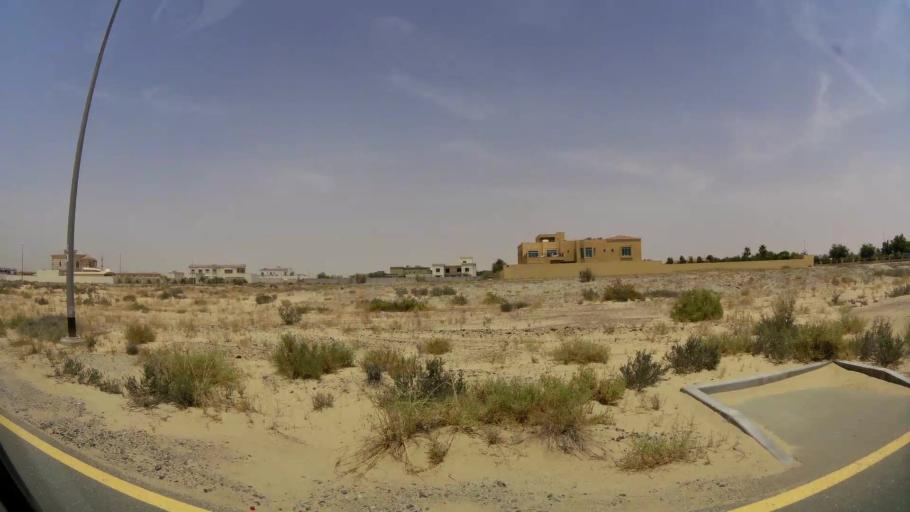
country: AE
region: Ash Shariqah
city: Sharjah
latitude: 25.2448
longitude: 55.4703
